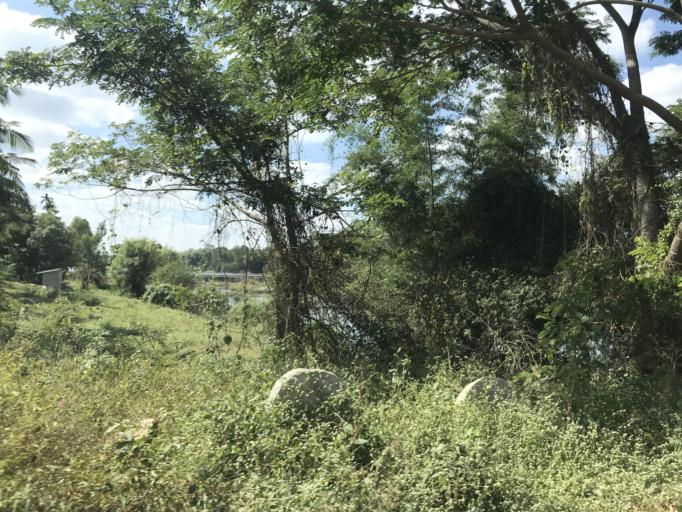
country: IN
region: Karnataka
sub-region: Mandya
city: Krishnarajpet
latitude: 12.7326
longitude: 76.3788
